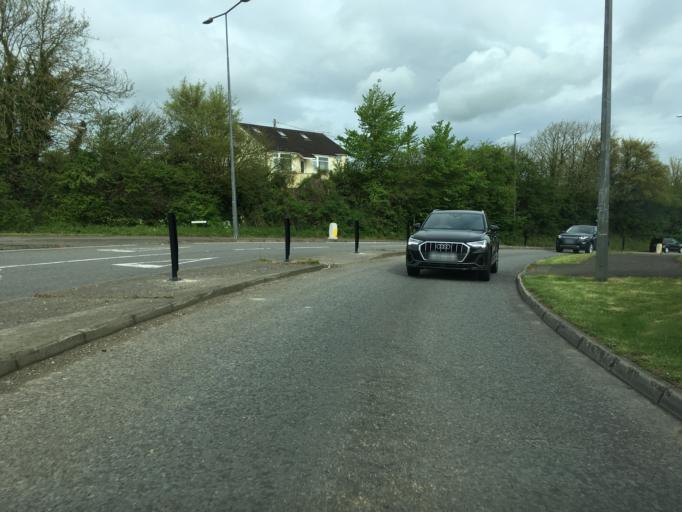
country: GB
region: England
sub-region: Bath and North East Somerset
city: Peasedown Saint John
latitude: 51.3229
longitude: -2.4169
